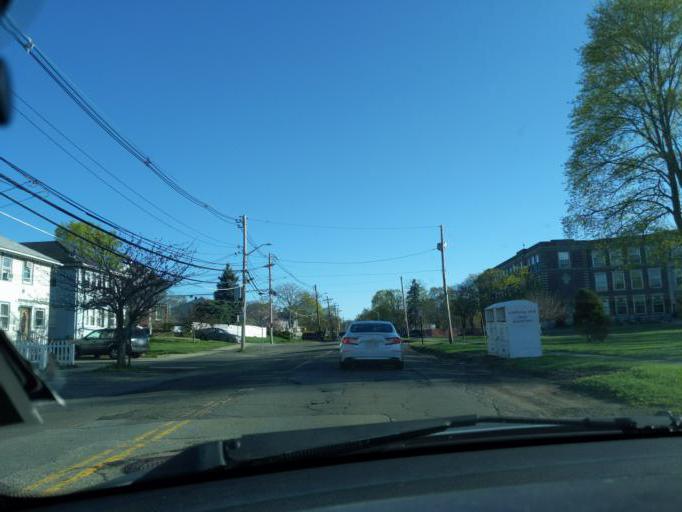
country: US
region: Massachusetts
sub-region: Essex County
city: Beverly
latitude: 42.5586
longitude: -70.8799
